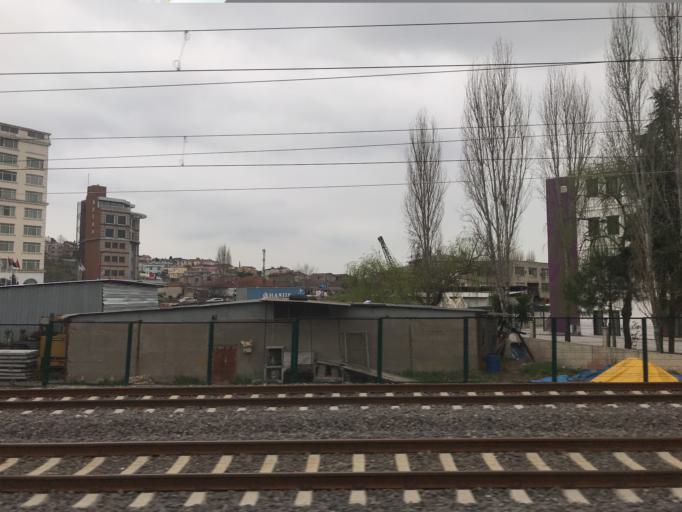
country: TR
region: Istanbul
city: Maltepe
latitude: 40.9164
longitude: 29.1436
